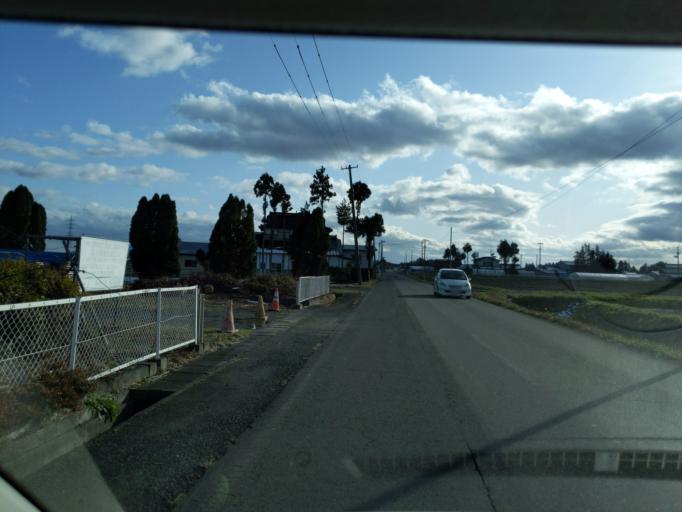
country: JP
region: Iwate
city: Mizusawa
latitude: 39.1471
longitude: 141.0787
